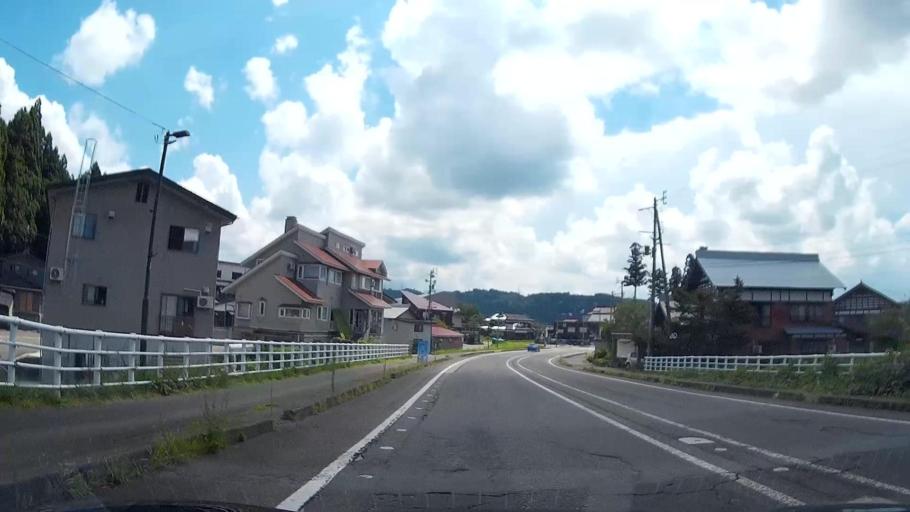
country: JP
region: Niigata
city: Tokamachi
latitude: 37.0497
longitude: 138.6936
